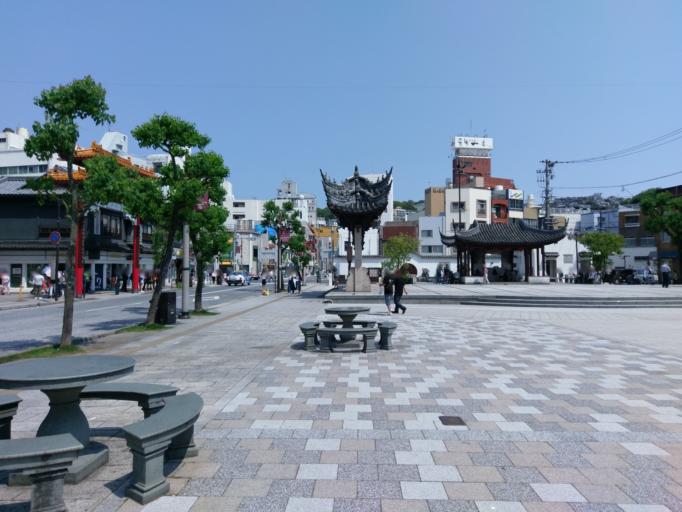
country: JP
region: Nagasaki
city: Nagasaki-shi
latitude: 32.7410
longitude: 129.8745
